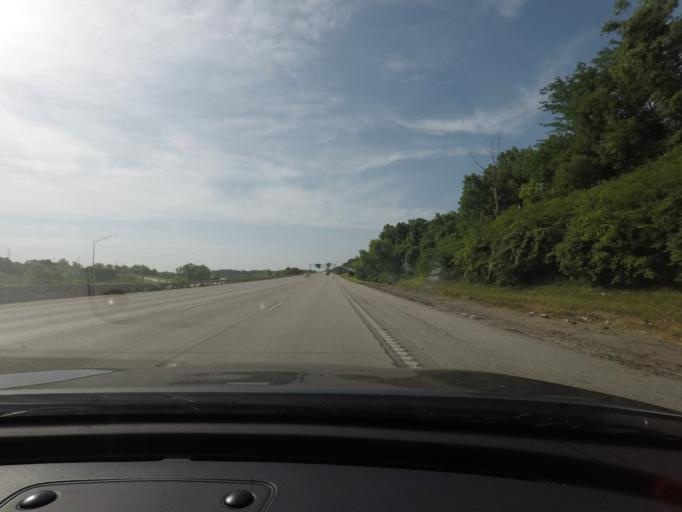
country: US
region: Missouri
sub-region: Saint Louis County
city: Bridgeton
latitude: 38.7742
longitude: -90.4116
